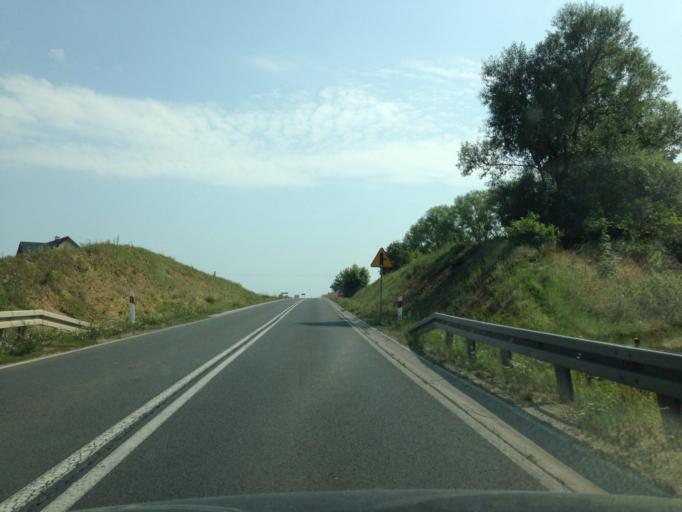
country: PL
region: Kujawsko-Pomorskie
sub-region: Powiat golubsko-dobrzynski
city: Radomin
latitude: 53.1021
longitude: 19.1331
